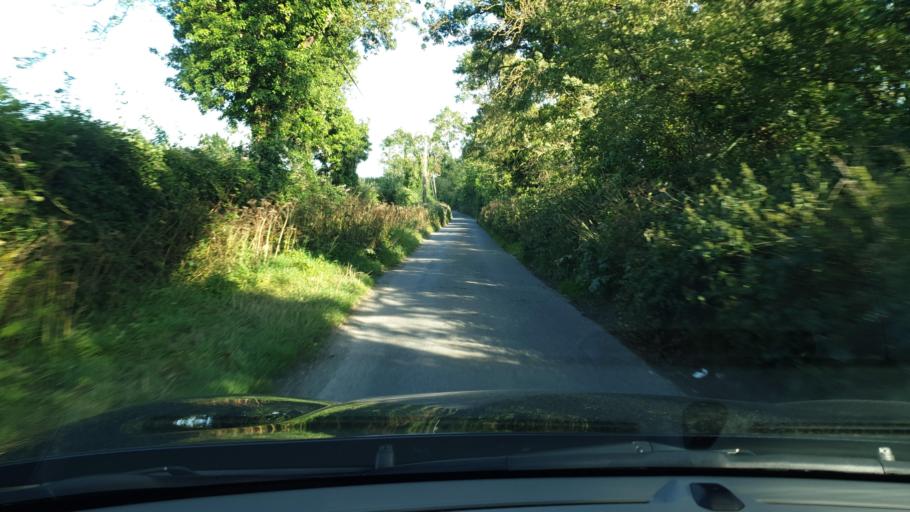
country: IE
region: Leinster
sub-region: An Mhi
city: Stamullin
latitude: 53.6002
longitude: -6.2686
